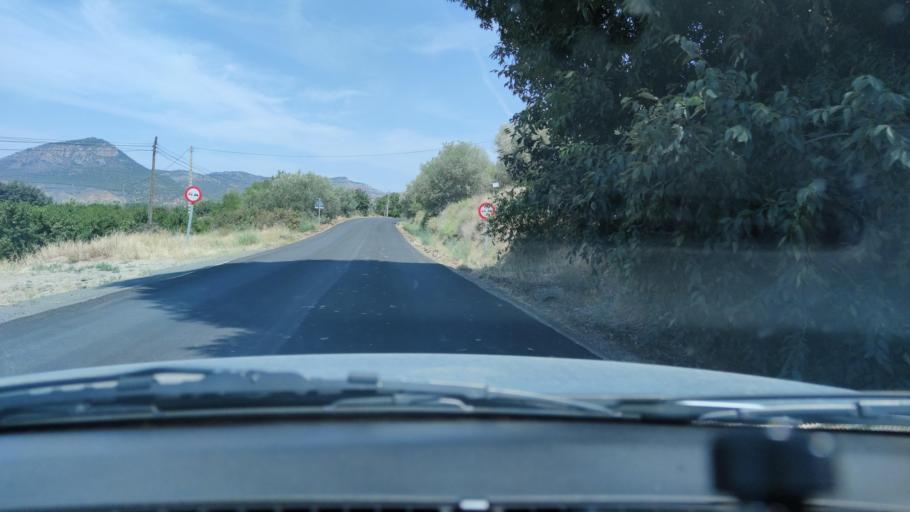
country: ES
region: Catalonia
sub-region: Provincia de Lleida
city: Alfarras
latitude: 41.8417
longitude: 0.5842
